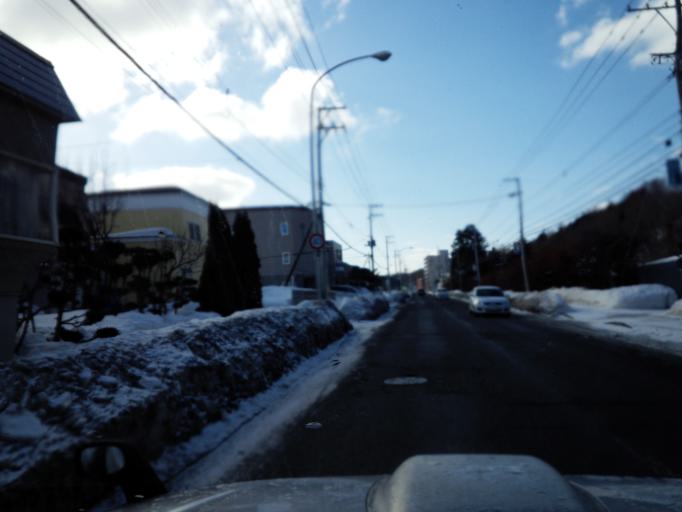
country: JP
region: Hokkaido
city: Sapporo
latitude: 42.9594
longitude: 141.3436
